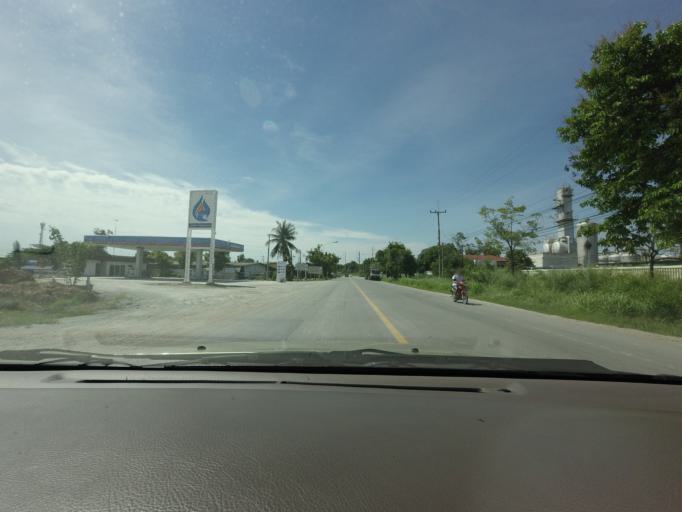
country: TH
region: Chon Buri
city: Chon Buri
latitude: 13.2758
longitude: 100.9657
